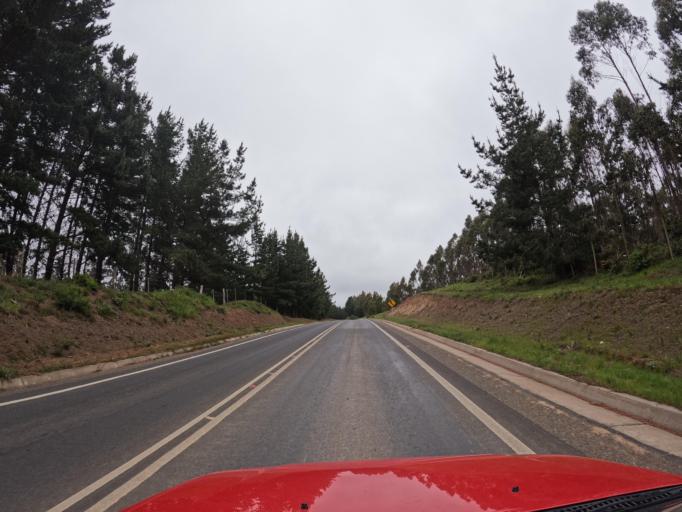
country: CL
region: O'Higgins
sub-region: Provincia de Colchagua
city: Santa Cruz
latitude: -34.6026
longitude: -72.0160
